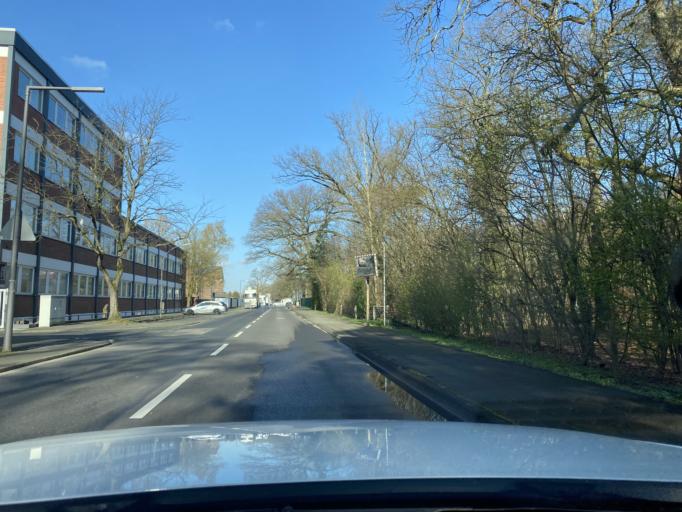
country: DE
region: North Rhine-Westphalia
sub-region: Regierungsbezirk Koln
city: Merheim
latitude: 50.9832
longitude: 7.0751
